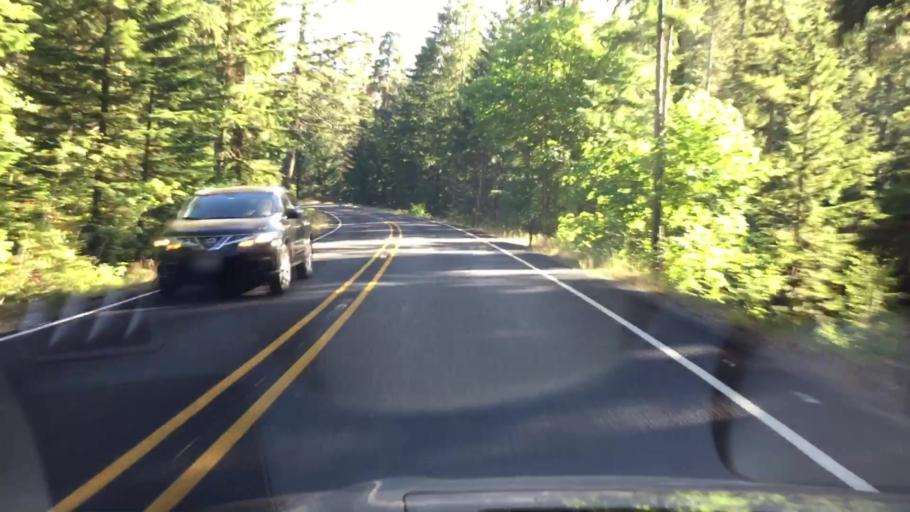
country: US
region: Washington
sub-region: Pierce County
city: Buckley
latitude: 46.7007
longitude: -121.5824
